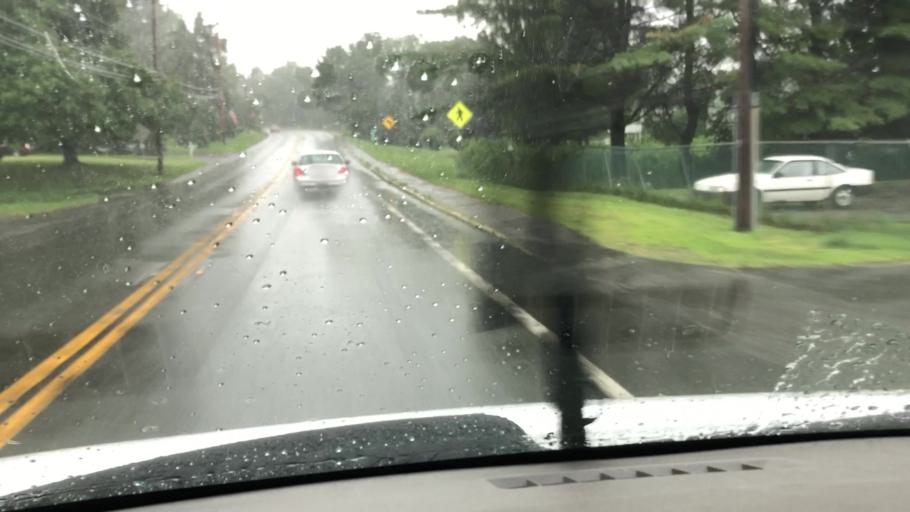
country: US
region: Massachusetts
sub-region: Berkshire County
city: Adams
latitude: 42.5676
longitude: -73.1596
